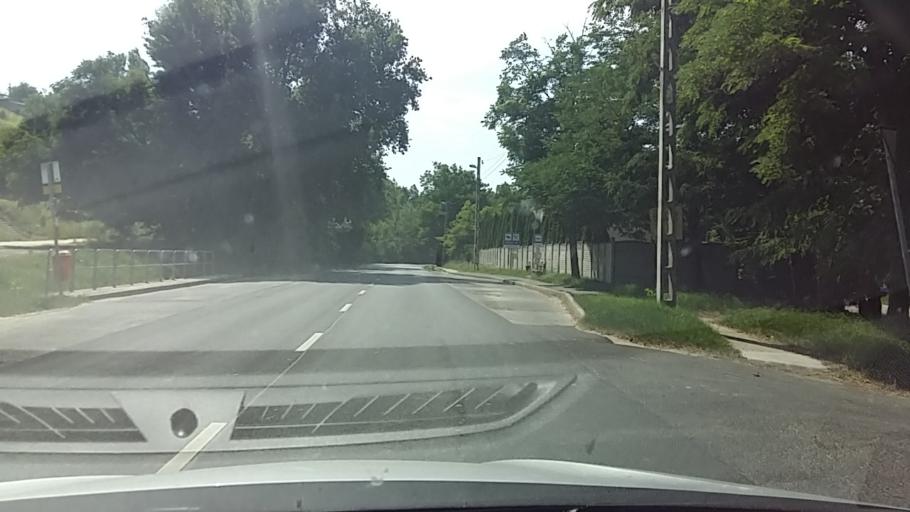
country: HU
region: Pest
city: Mogyorod
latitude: 47.6000
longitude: 19.2552
